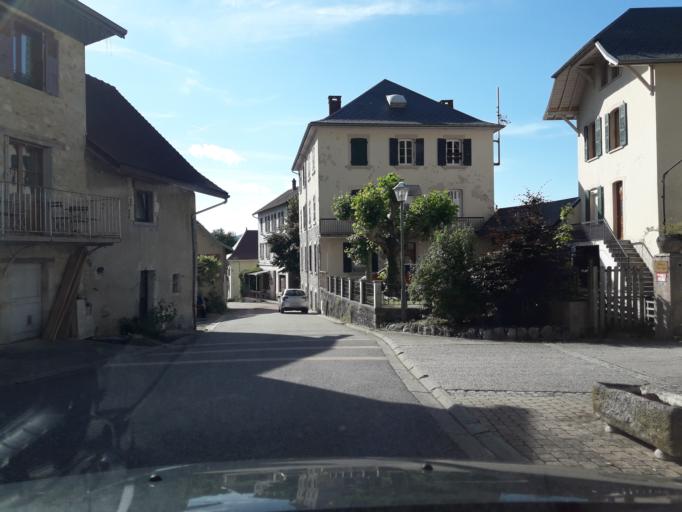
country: FR
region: Rhone-Alpes
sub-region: Departement de la Savoie
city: Vimines
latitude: 45.5375
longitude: 5.8149
